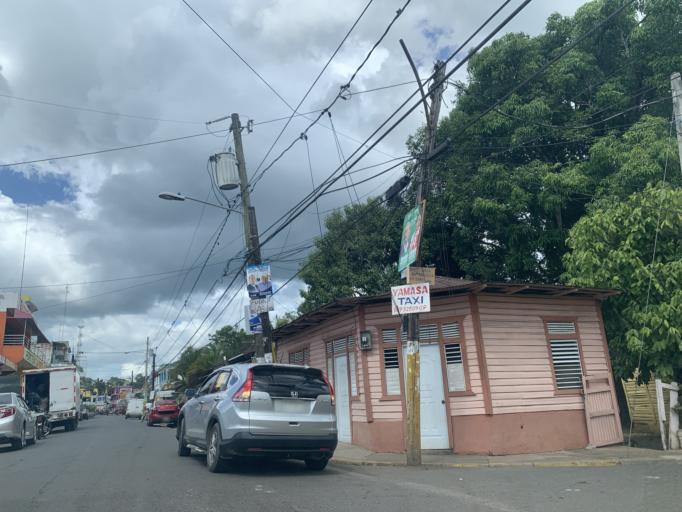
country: DO
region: Monte Plata
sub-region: Yamasa
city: Yamasa
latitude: 18.7710
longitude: -70.0249
